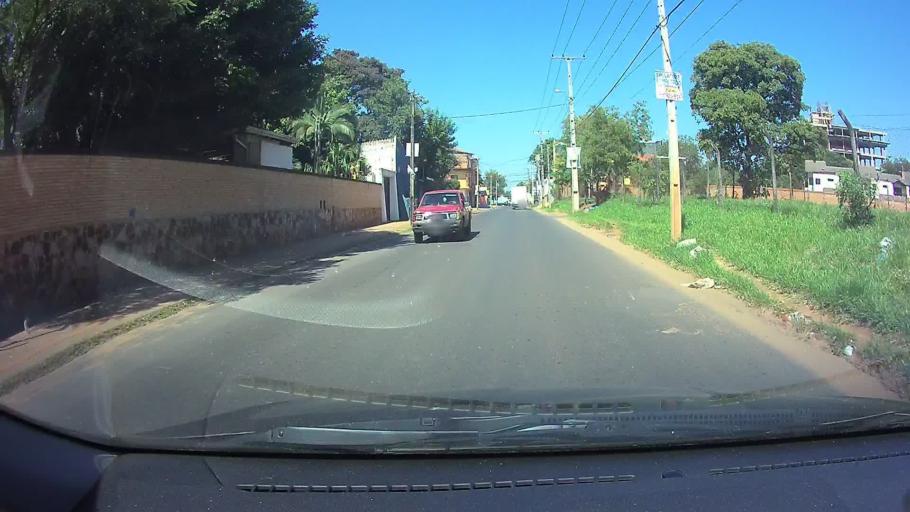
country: PY
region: Central
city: Fernando de la Mora
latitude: -25.3186
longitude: -57.5216
